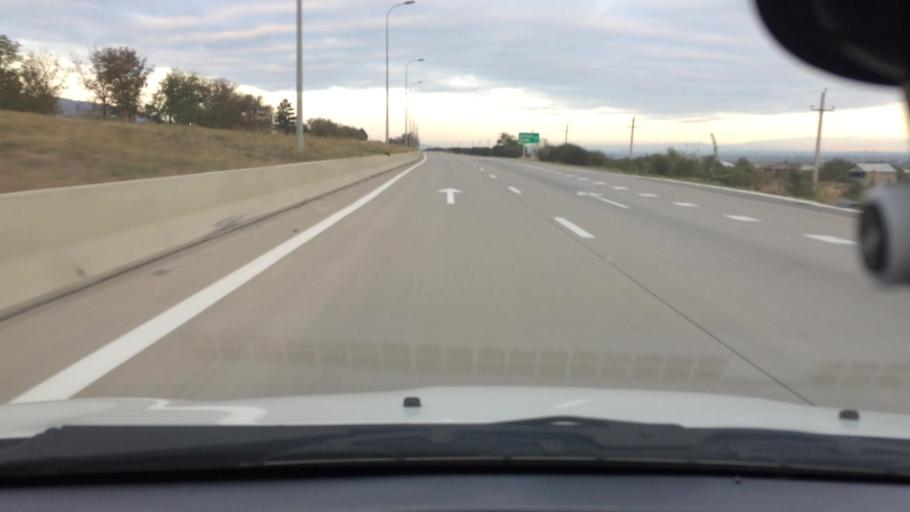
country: GE
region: Shida Kartli
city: Kaspi
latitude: 42.0228
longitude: 44.2838
